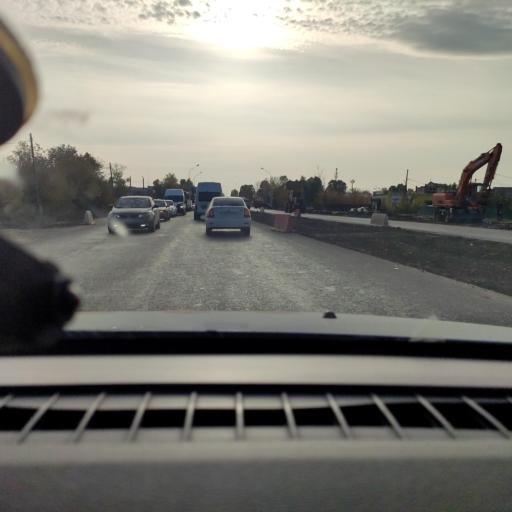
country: RU
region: Samara
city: Samara
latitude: 53.1337
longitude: 50.0995
